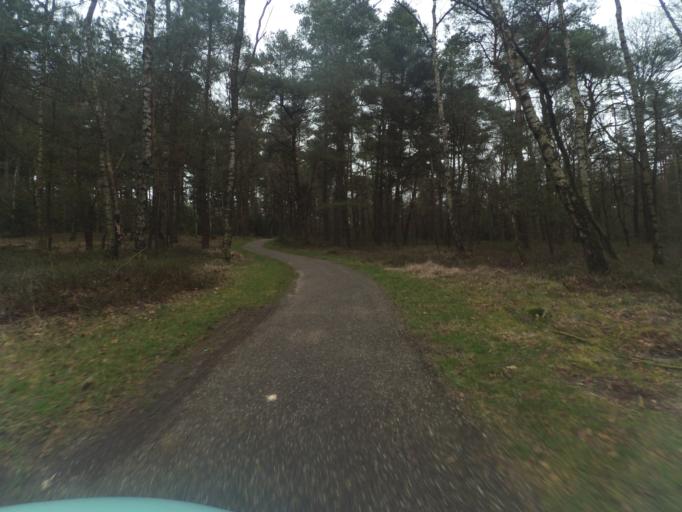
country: NL
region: Gelderland
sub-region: Gemeente Apeldoorn
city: Loenen
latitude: 52.0862
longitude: 6.0159
